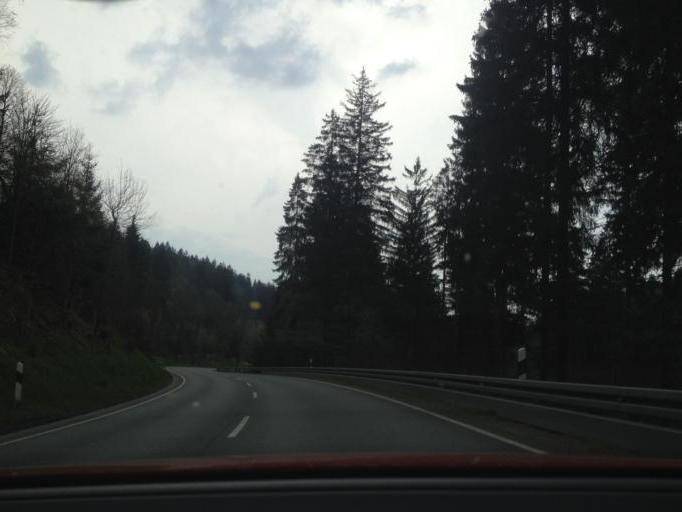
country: DE
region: Bavaria
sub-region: Upper Franconia
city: Bischofsgrun
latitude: 50.0490
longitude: 11.7536
